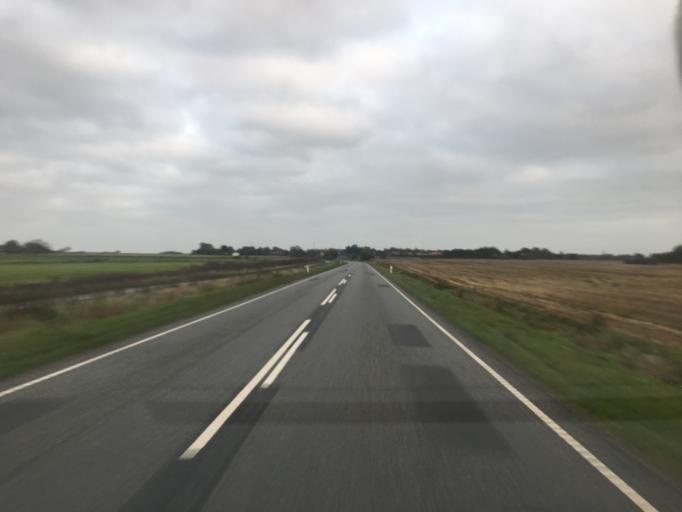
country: DE
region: Schleswig-Holstein
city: Aventoft
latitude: 54.9522
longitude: 8.7814
